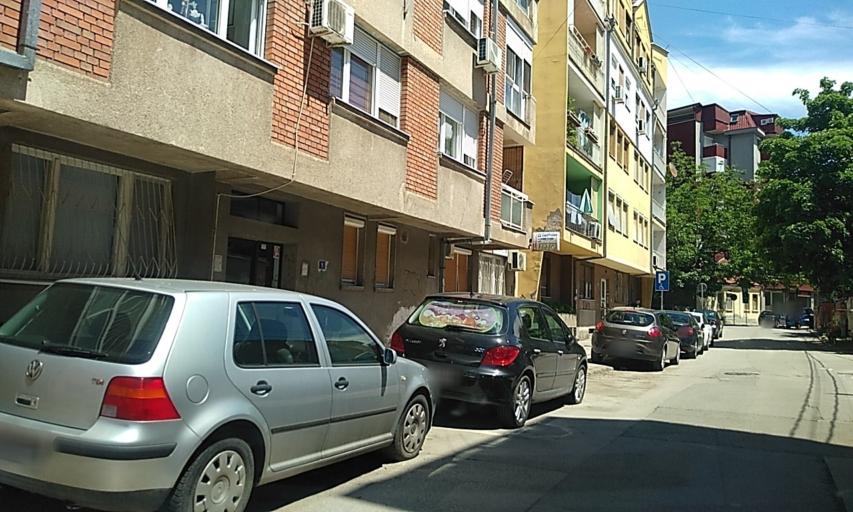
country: RS
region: Central Serbia
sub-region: Nisavski Okrug
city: Nis
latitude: 43.3158
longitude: 21.8923
